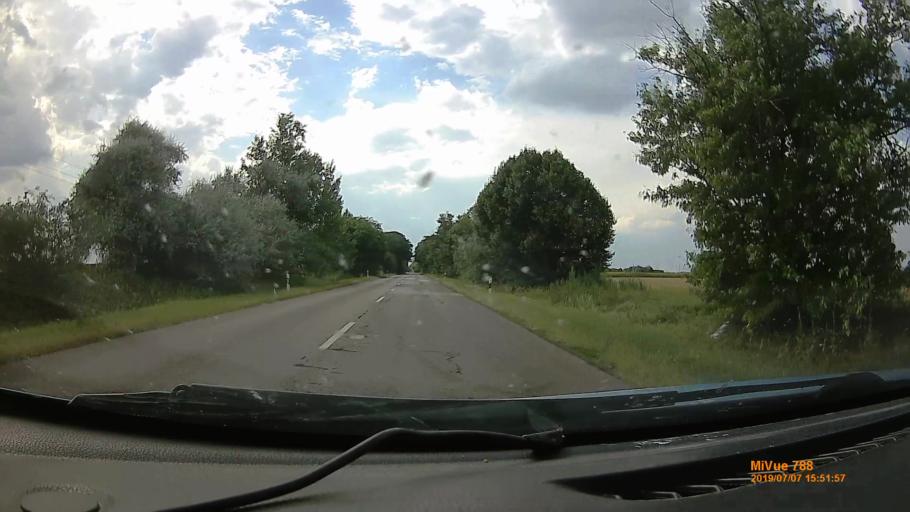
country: HU
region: Pest
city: Szentlorinckata
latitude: 47.5374
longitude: 19.8310
